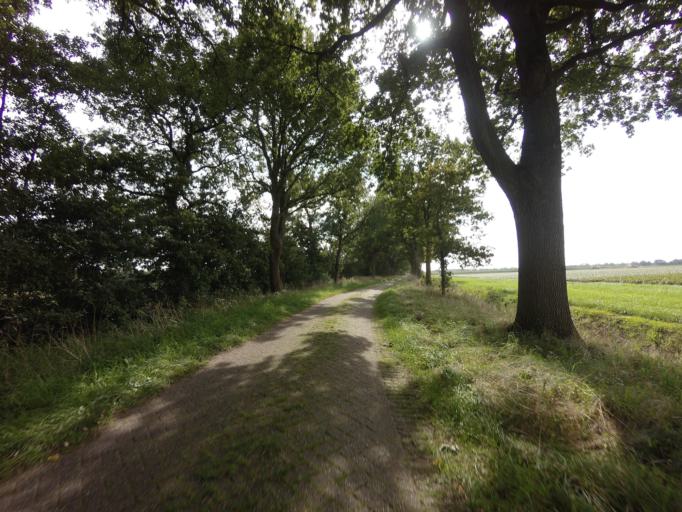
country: NL
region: Drenthe
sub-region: Gemeente Coevorden
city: Sleen
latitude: 52.7859
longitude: 6.7270
